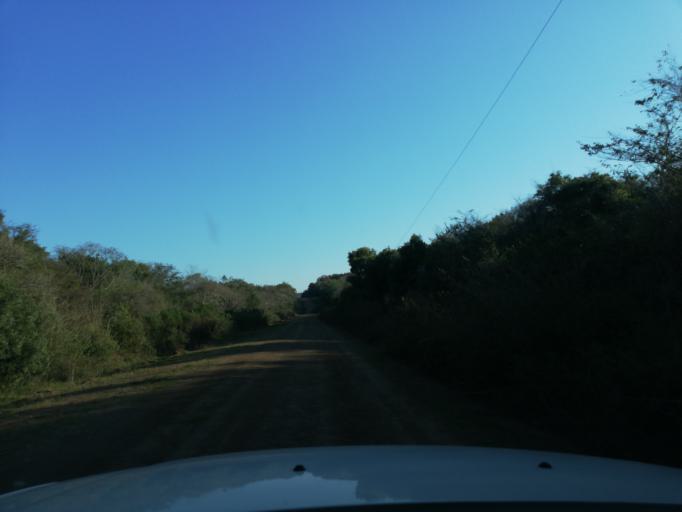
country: AR
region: Misiones
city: Cerro Cora
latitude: -27.5914
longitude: -55.6923
